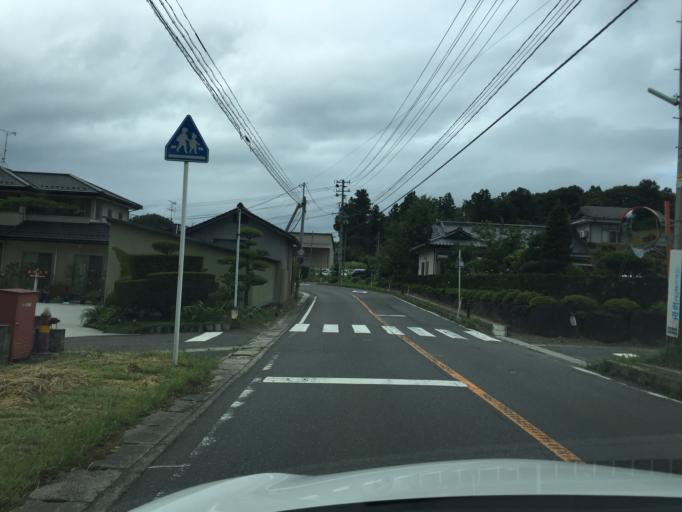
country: JP
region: Fukushima
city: Funehikimachi-funehiki
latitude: 37.4624
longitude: 140.5745
